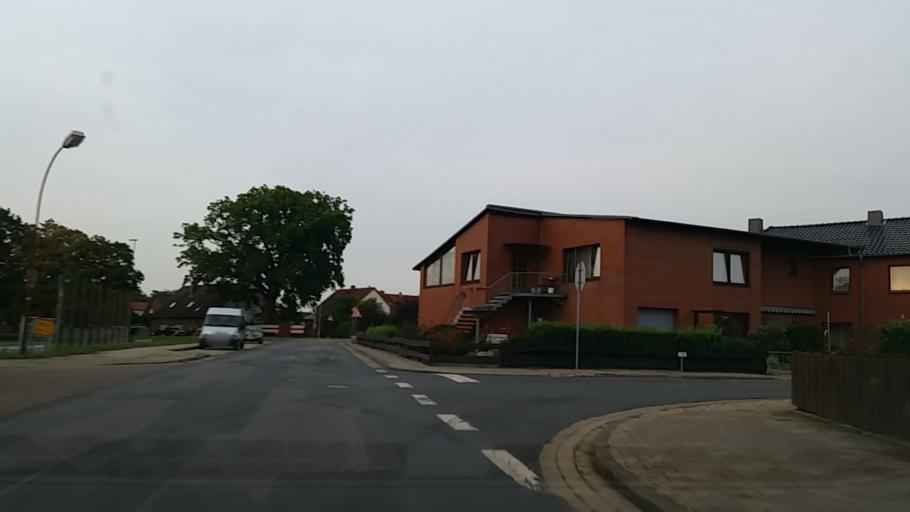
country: DE
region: Lower Saxony
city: Vordorf
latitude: 52.3639
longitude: 10.5225
